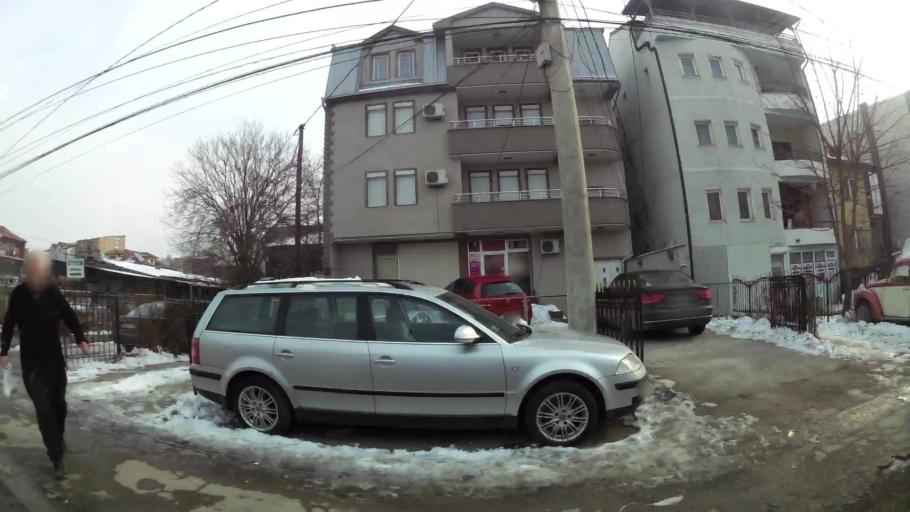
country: MK
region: Cair
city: Cair
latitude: 42.0123
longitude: 21.4419
